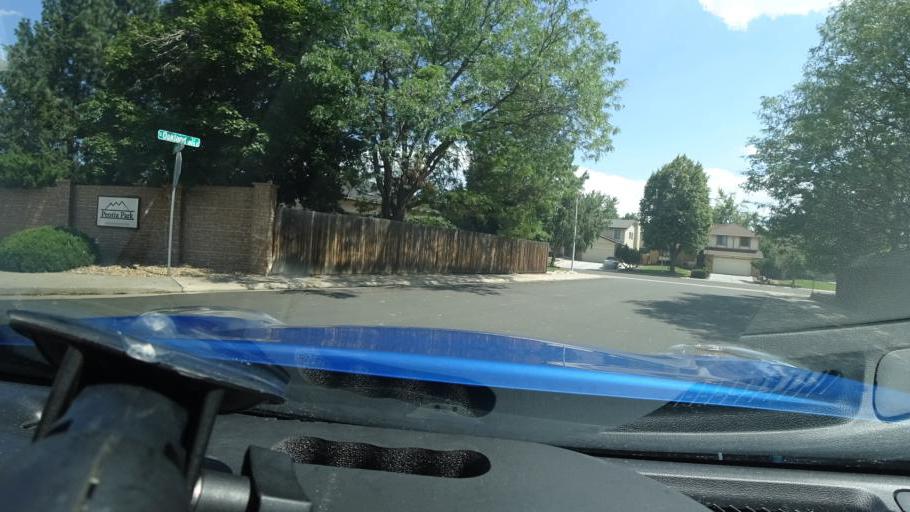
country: US
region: Colorado
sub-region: Adams County
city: Aurora
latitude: 39.6820
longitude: -104.8507
